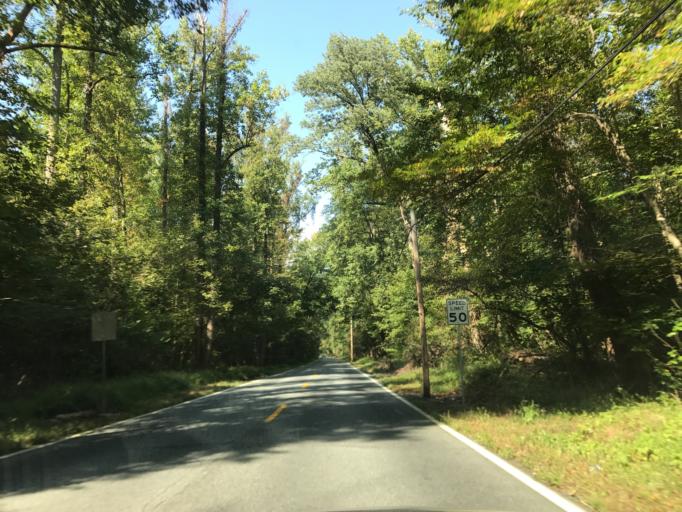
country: US
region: Maryland
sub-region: Harford County
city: Havre de Grace
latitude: 39.6374
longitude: -76.1488
